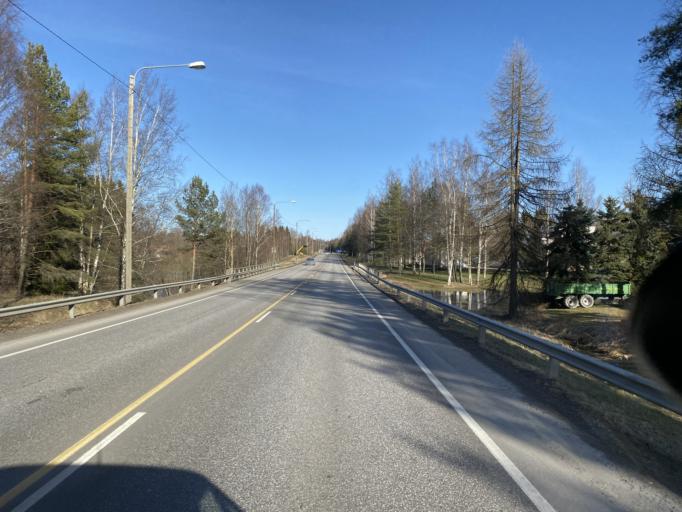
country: FI
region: Satakunta
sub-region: Rauma
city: Eura
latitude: 61.1313
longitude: 22.1317
